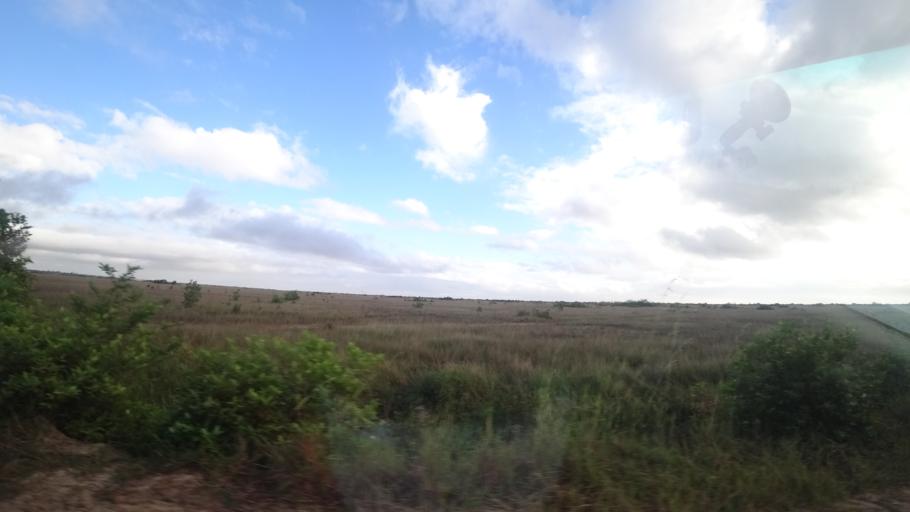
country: MZ
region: Sofala
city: Beira
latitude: -19.7056
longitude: 35.0193
